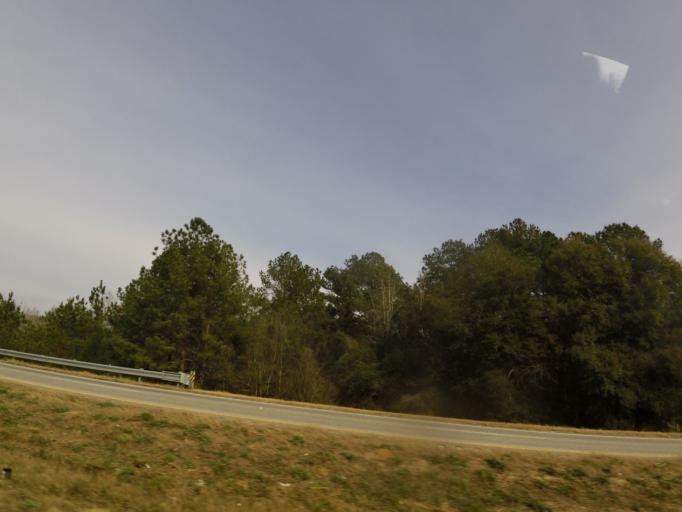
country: US
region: Alabama
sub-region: Dale County
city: Midland City
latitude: 31.3386
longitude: -85.5460
